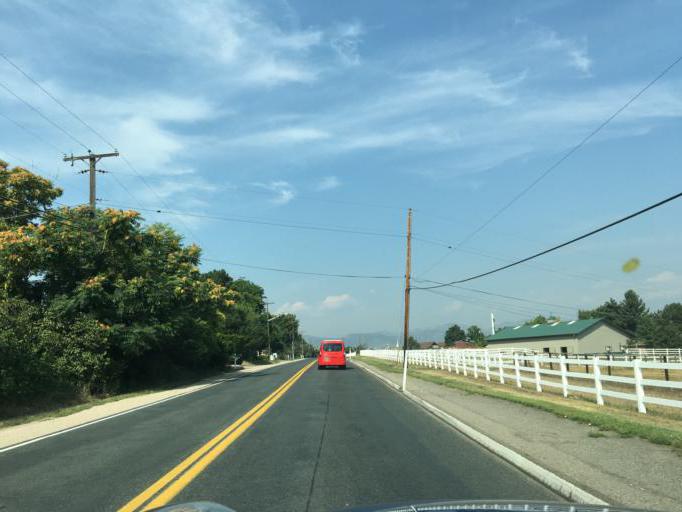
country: US
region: Colorado
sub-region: Jefferson County
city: Arvada
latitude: 39.8421
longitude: -105.1244
